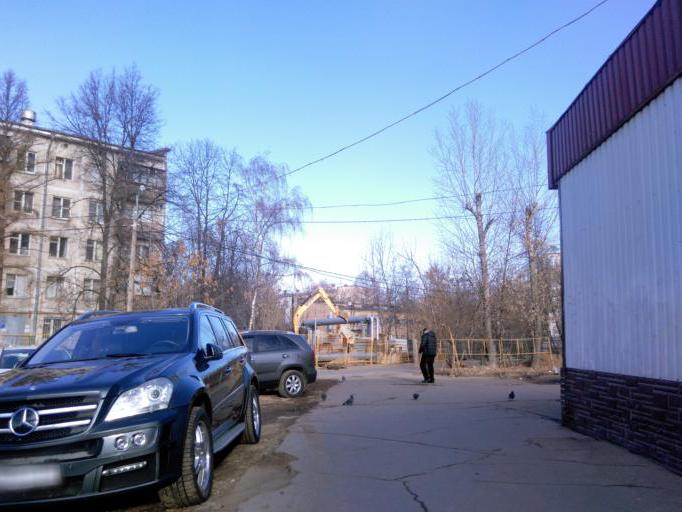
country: RU
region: Moscow
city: Nikol'skoye
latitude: 55.6726
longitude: 37.5075
